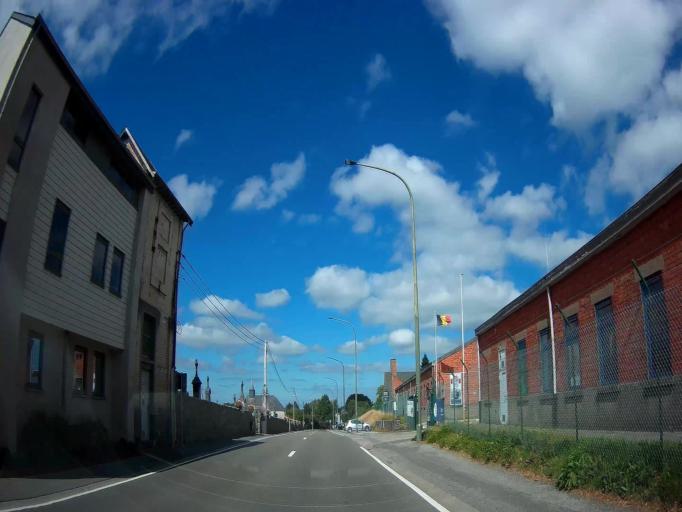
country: BE
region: Wallonia
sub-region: Province du Luxembourg
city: Bastogne
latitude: 50.0080
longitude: 5.7187
